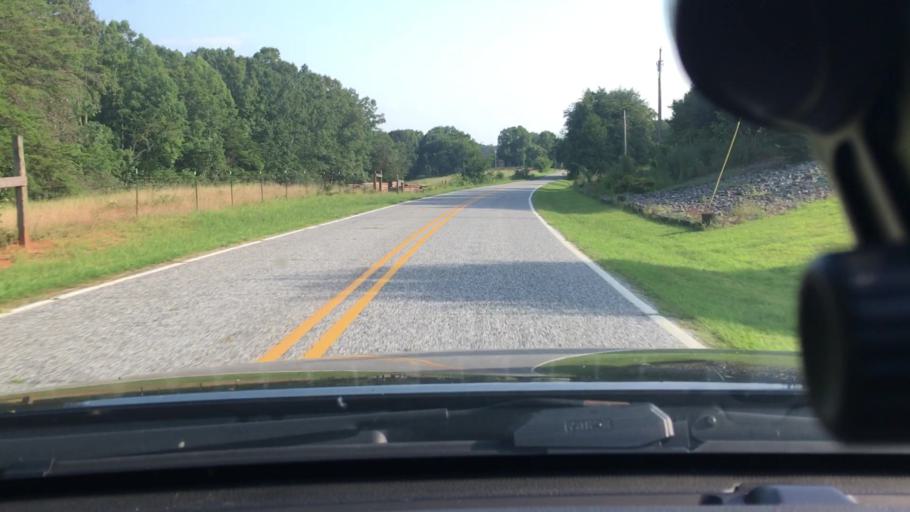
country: US
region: North Carolina
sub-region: Rutherford County
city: Rutherfordton
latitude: 35.3857
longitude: -81.9850
